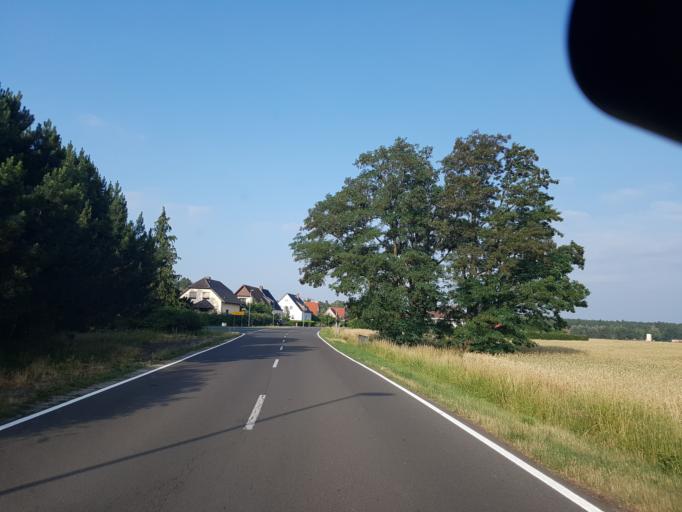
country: DE
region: Saxony-Anhalt
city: Holzdorf
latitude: 51.8549
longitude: 13.0953
